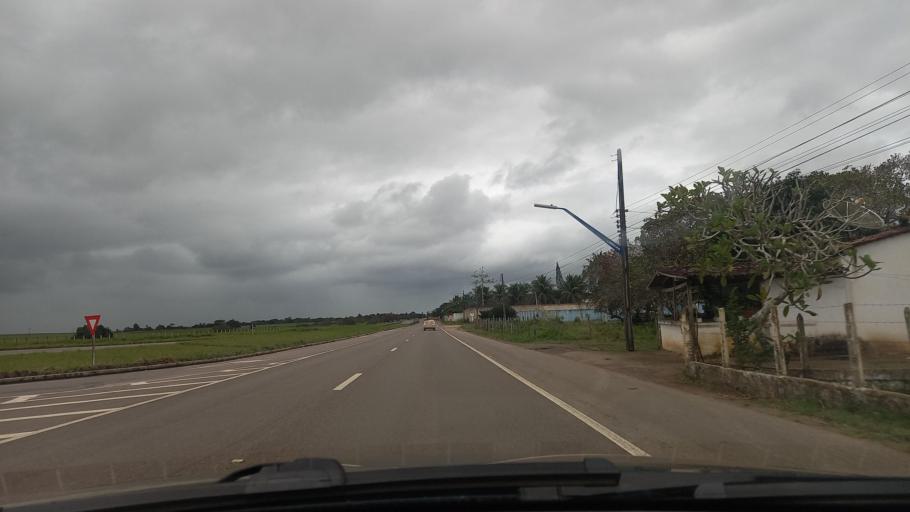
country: BR
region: Alagoas
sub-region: Limoeiro De Anadia
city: Cajueiro
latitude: -9.7468
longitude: -36.4604
